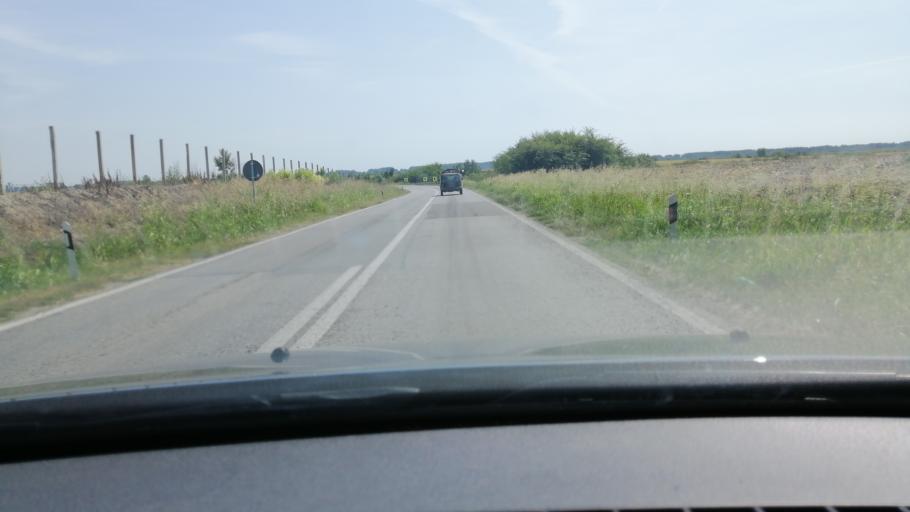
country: RS
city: Sutjeska
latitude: 45.3781
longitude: 20.7308
